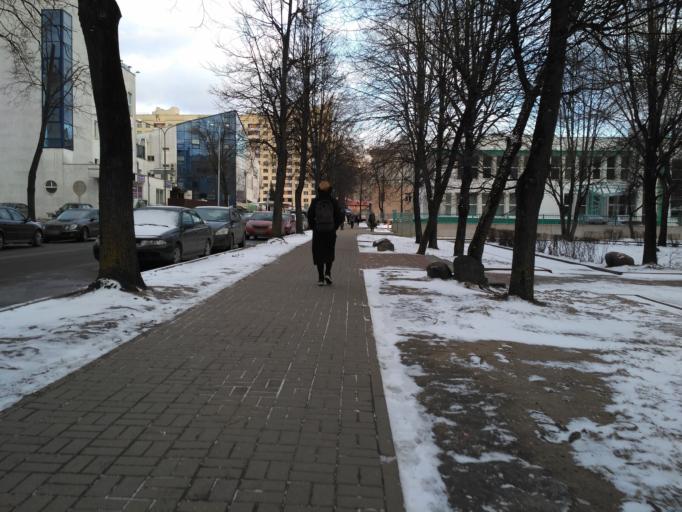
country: BY
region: Minsk
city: Minsk
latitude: 53.9262
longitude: 27.5906
